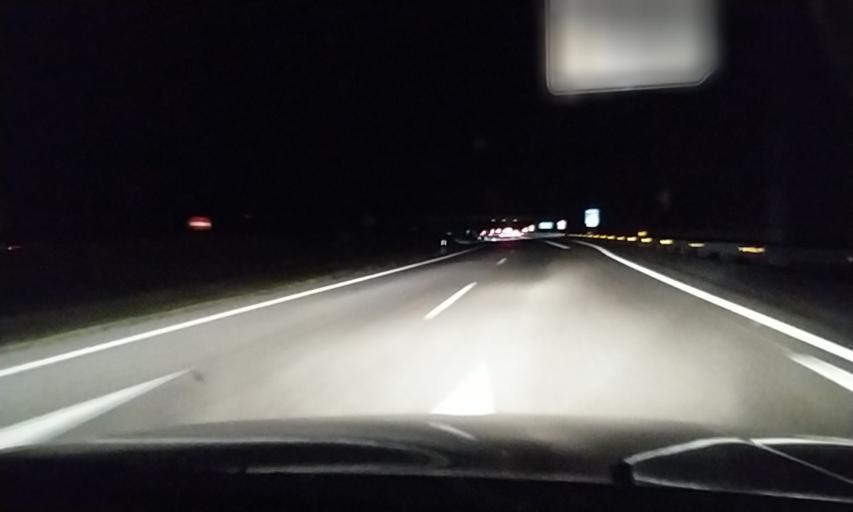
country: ES
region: Castille and Leon
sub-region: Provincia de Zamora
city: Pobladura del Valle
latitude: 42.1190
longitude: -5.7495
